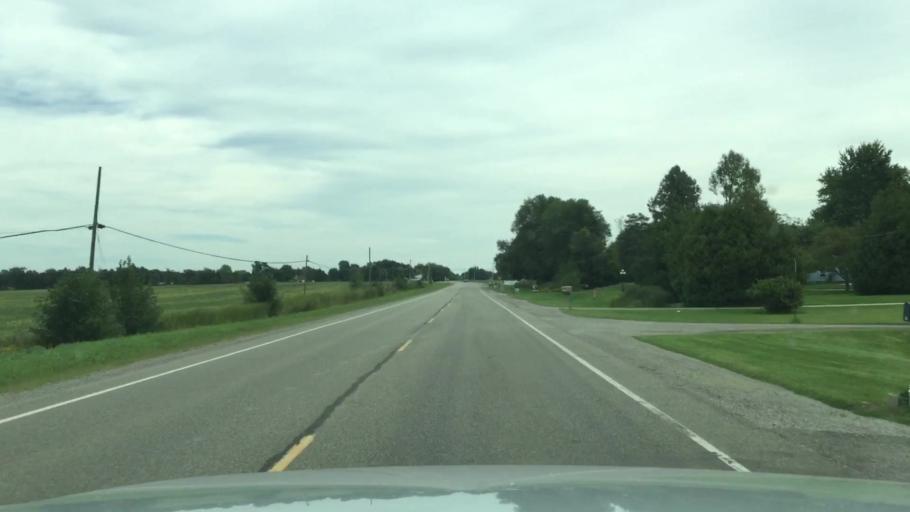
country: US
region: Michigan
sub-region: Shiawassee County
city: Durand
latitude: 42.9255
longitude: -83.9738
